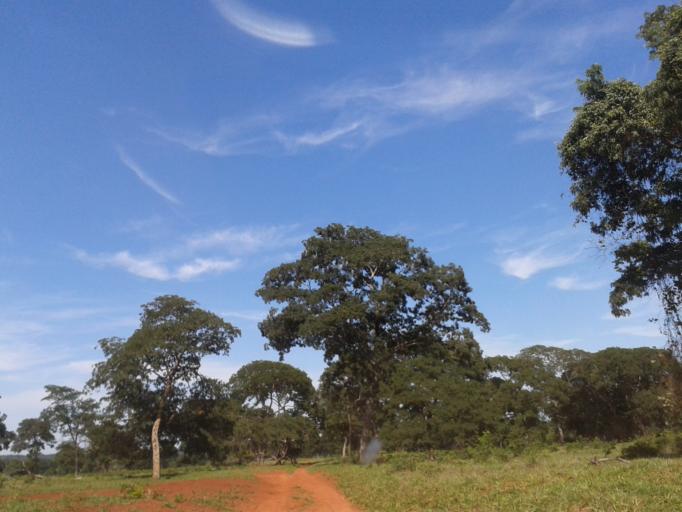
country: BR
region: Minas Gerais
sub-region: Santa Vitoria
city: Santa Vitoria
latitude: -19.1636
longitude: -50.5129
